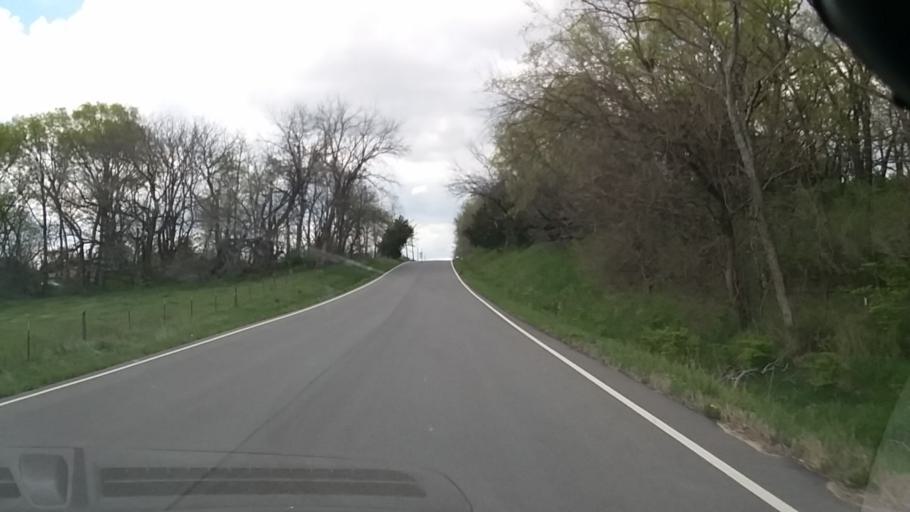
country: US
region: Kansas
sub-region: Douglas County
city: Lawrence
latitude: 38.8911
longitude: -95.2418
